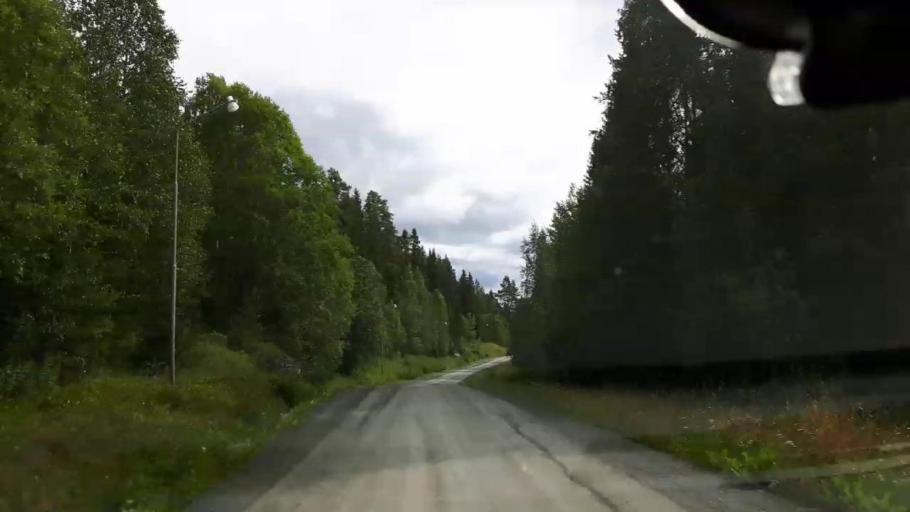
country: SE
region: Jaemtland
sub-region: Krokoms Kommun
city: Valla
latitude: 63.6209
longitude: 14.0595
